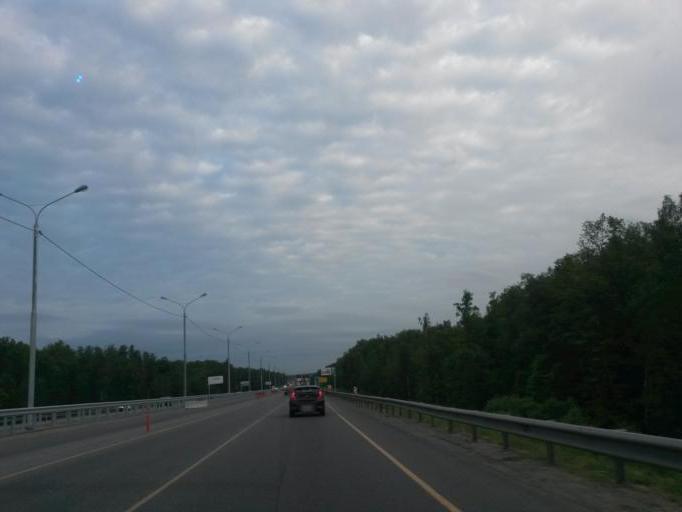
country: RU
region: Moskovskaya
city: Lyubuchany
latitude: 55.2044
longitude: 37.5351
